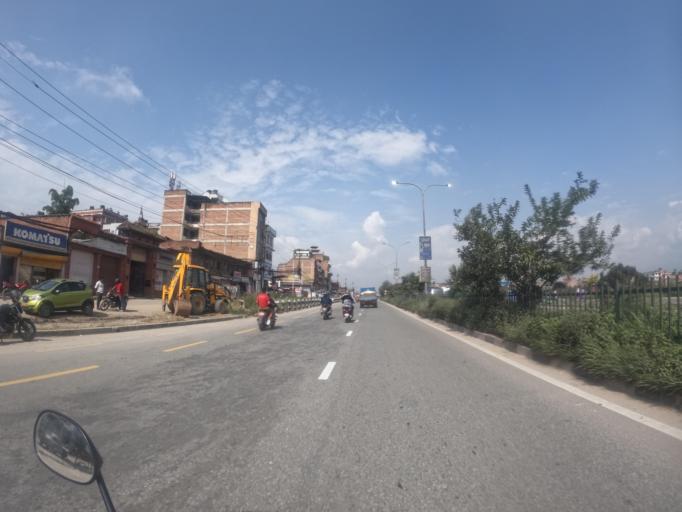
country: NP
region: Central Region
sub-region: Bagmati Zone
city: Bhaktapur
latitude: 27.6721
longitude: 85.4071
